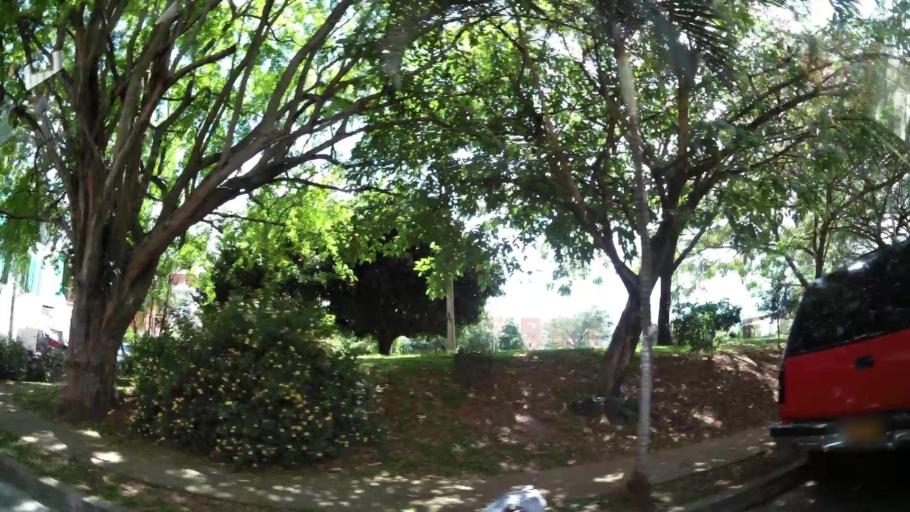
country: CO
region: Valle del Cauca
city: Cali
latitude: 3.3939
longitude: -76.5172
